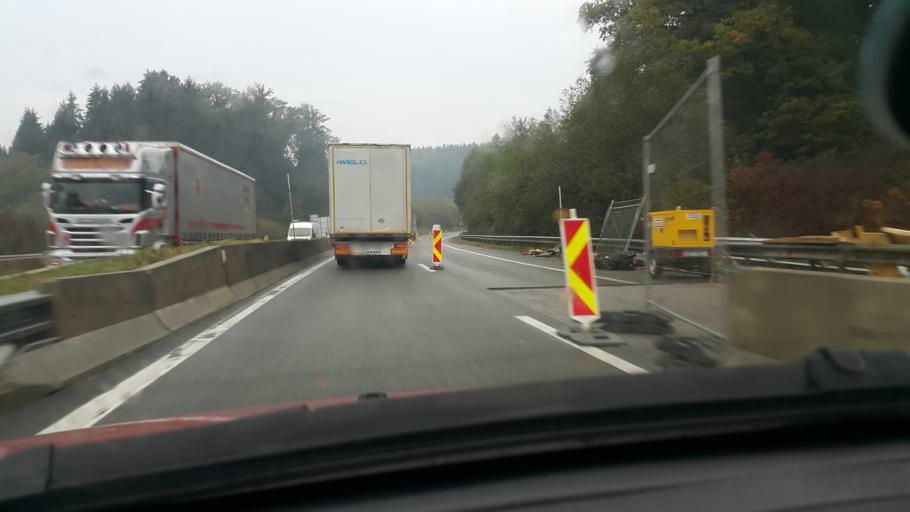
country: AT
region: Carinthia
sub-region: Politischer Bezirk Volkermarkt
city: Voelkermarkt
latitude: 46.6447
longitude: 14.5527
